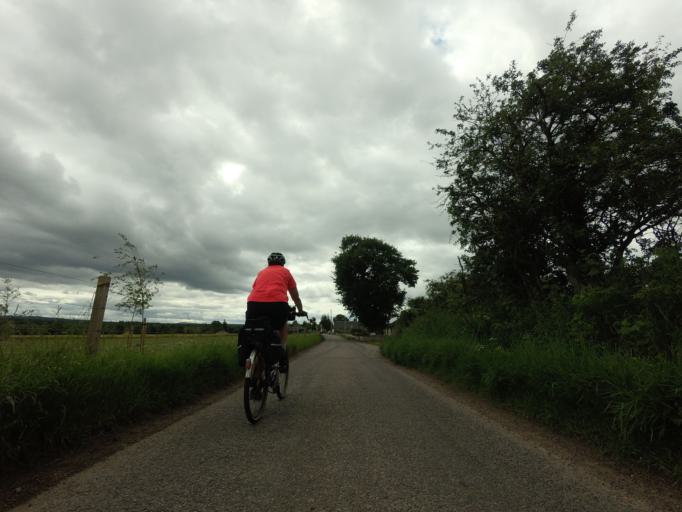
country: GB
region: Scotland
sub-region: Moray
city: Forres
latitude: 57.6076
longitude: -3.6913
